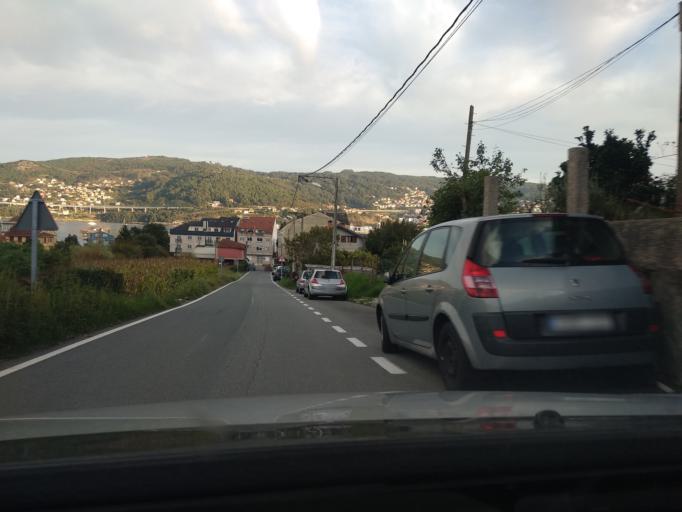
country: ES
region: Galicia
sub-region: Provincia de Pontevedra
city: Moana
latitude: 42.2868
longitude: -8.6848
